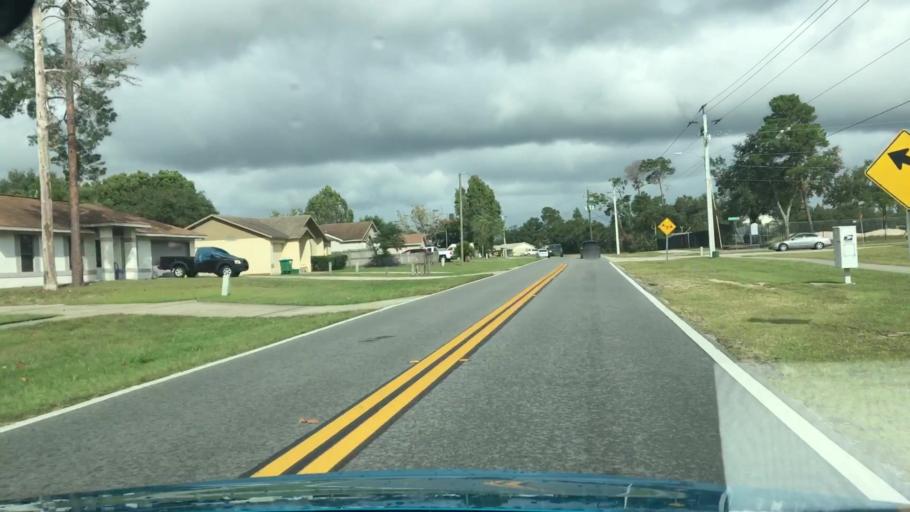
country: US
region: Florida
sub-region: Volusia County
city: Lake Helen
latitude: 28.9402
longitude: -81.1807
